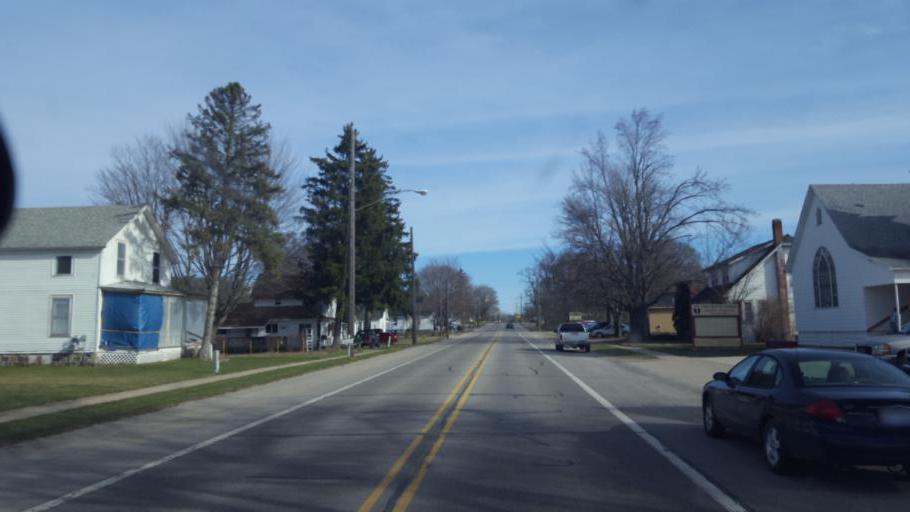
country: US
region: Michigan
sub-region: Montcalm County
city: Howard City
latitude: 43.4924
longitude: -85.4448
